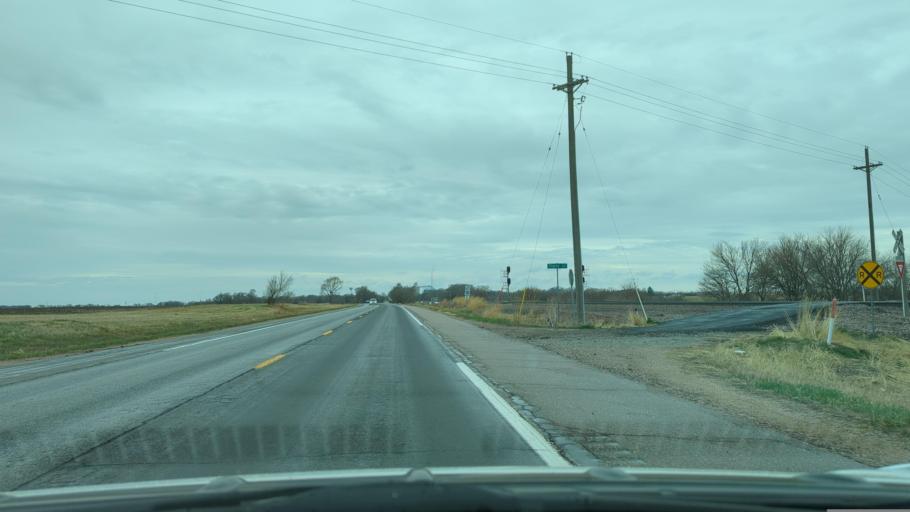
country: US
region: Nebraska
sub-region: Saunders County
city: Ashland
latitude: 40.9760
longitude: -96.4281
